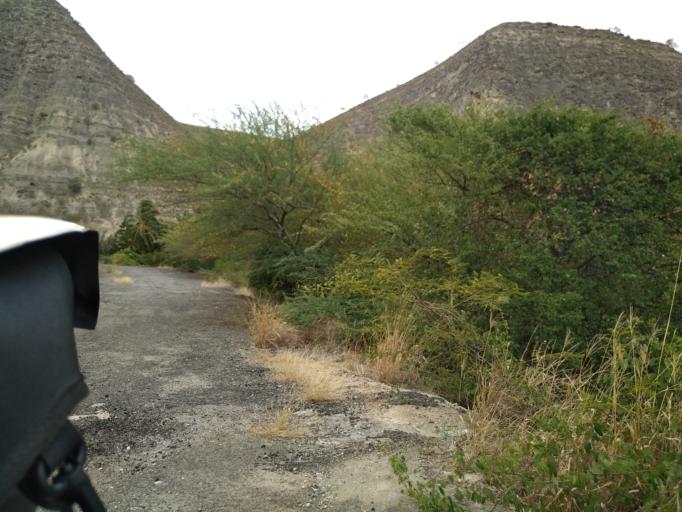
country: PE
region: Cajamarca
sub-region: Provincia de Jaen
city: Bellavista
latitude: -5.7547
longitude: -78.6919
